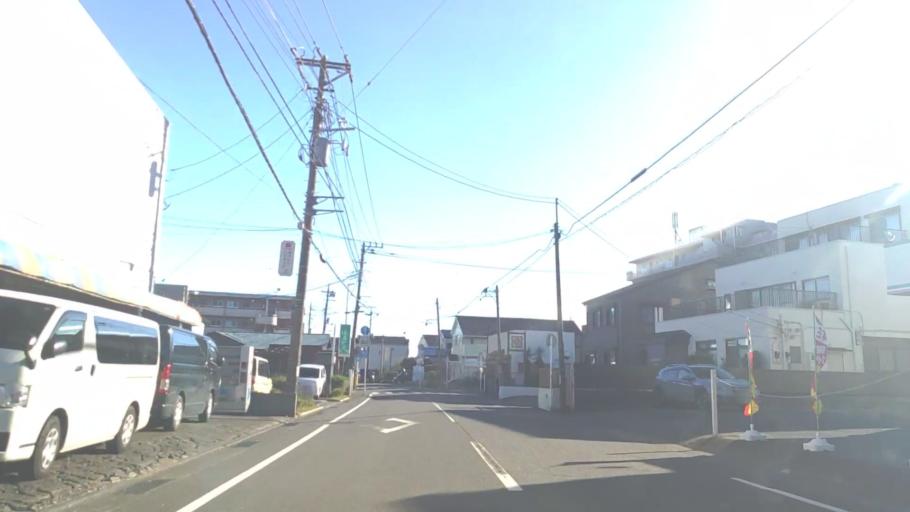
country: JP
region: Kanagawa
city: Atsugi
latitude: 35.3822
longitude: 139.3649
